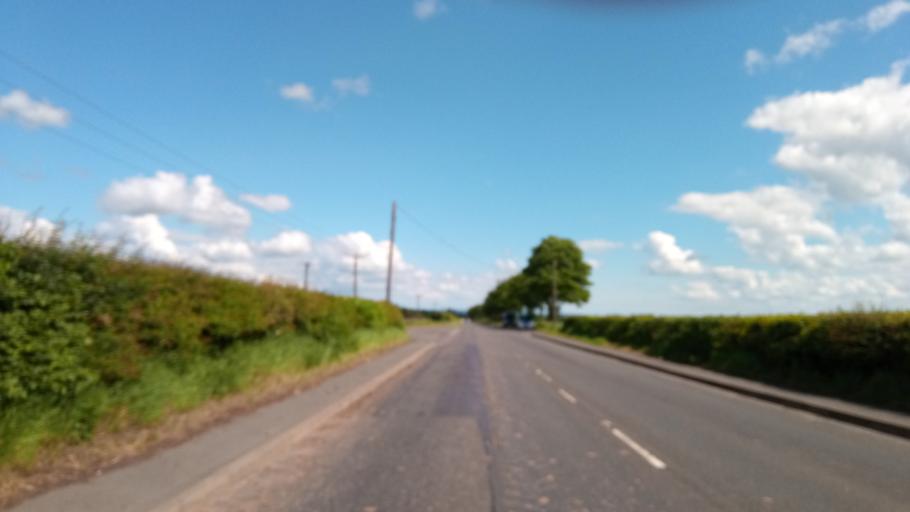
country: GB
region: Scotland
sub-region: The Scottish Borders
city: Kelso
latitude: 55.5822
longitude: -2.4460
